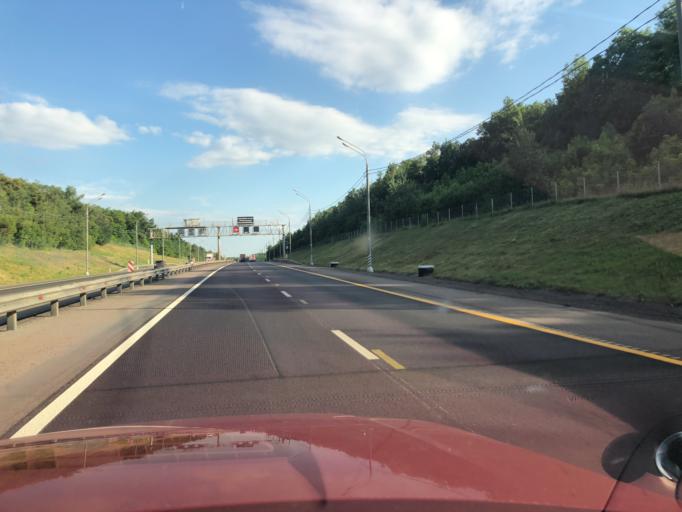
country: RU
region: Lipetsk
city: Zadonsk
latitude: 52.4009
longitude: 38.8587
